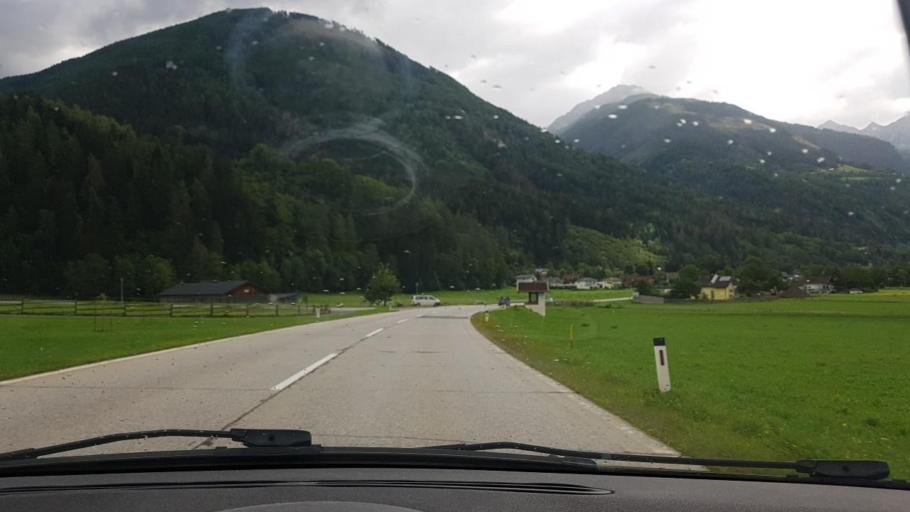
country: AT
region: Carinthia
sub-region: Politischer Bezirk Spittal an der Drau
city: Obervellach
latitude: 46.9384
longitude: 13.1750
